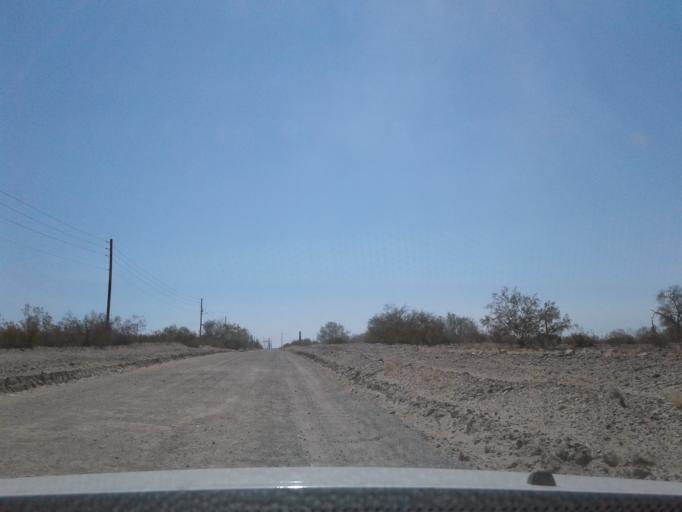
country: US
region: Arizona
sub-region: Maricopa County
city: Laveen
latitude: 33.2904
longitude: -112.1479
